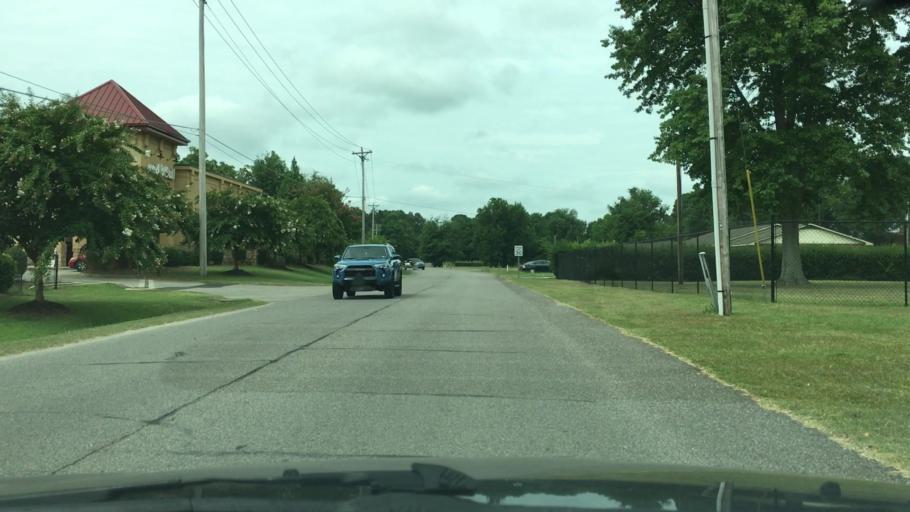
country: US
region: South Carolina
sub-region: Aiken County
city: Aiken
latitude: 33.5038
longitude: -81.7084
